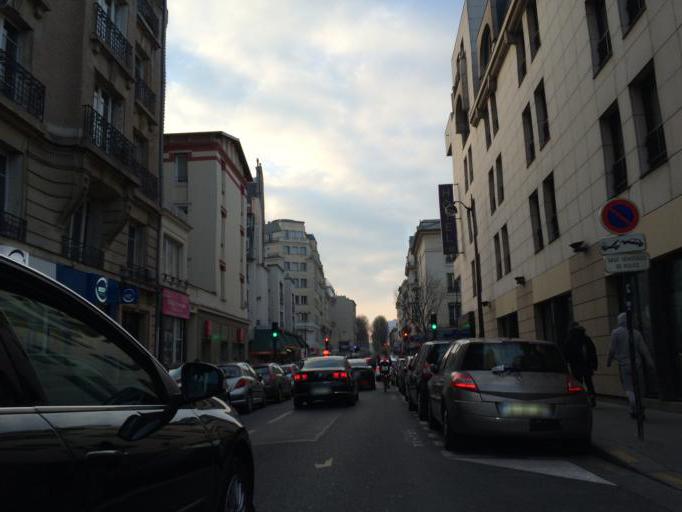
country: FR
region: Ile-de-France
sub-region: Paris
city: Paris
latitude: 48.8809
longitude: 2.3658
